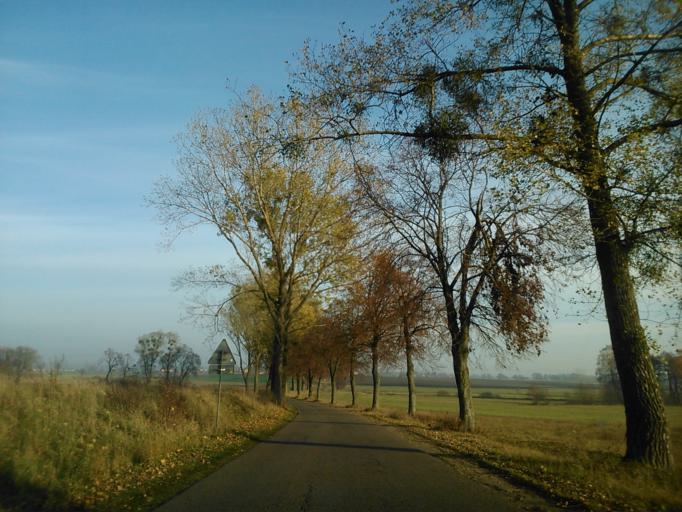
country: PL
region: Warmian-Masurian Voivodeship
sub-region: Powiat dzialdowski
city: Rybno
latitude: 53.2748
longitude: 19.9822
